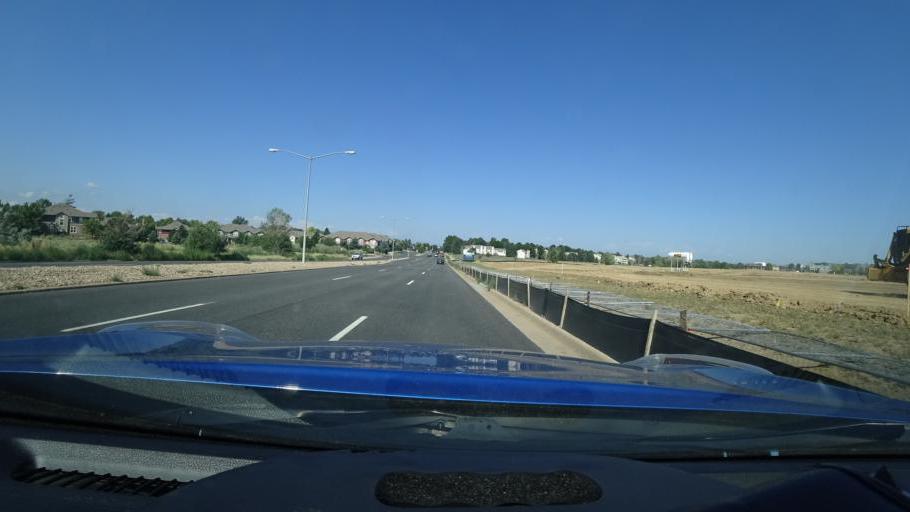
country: US
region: Colorado
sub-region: Adams County
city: Aurora
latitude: 39.7067
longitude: -104.7939
